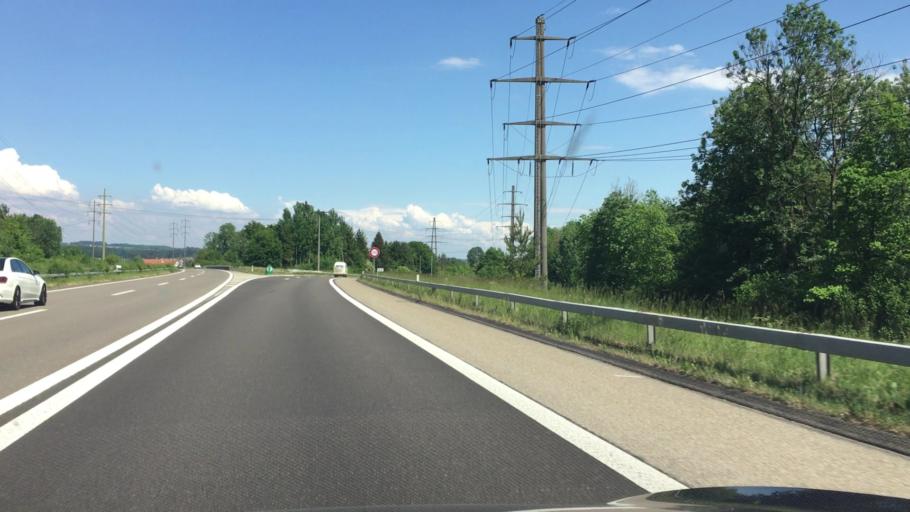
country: CH
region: Thurgau
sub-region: Frauenfeld District
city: Mullheim
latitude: 47.5892
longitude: 8.9946
